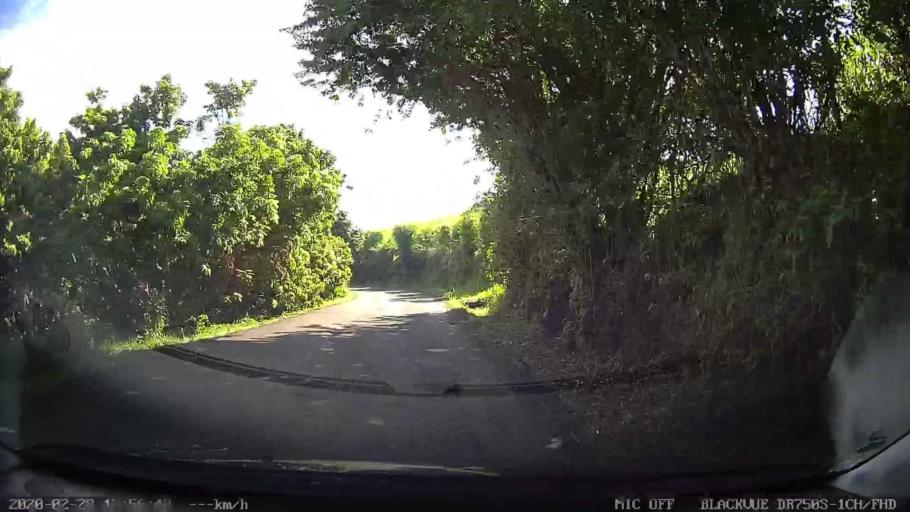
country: RE
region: Reunion
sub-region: Reunion
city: Sainte-Marie
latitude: -20.9385
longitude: 55.5252
